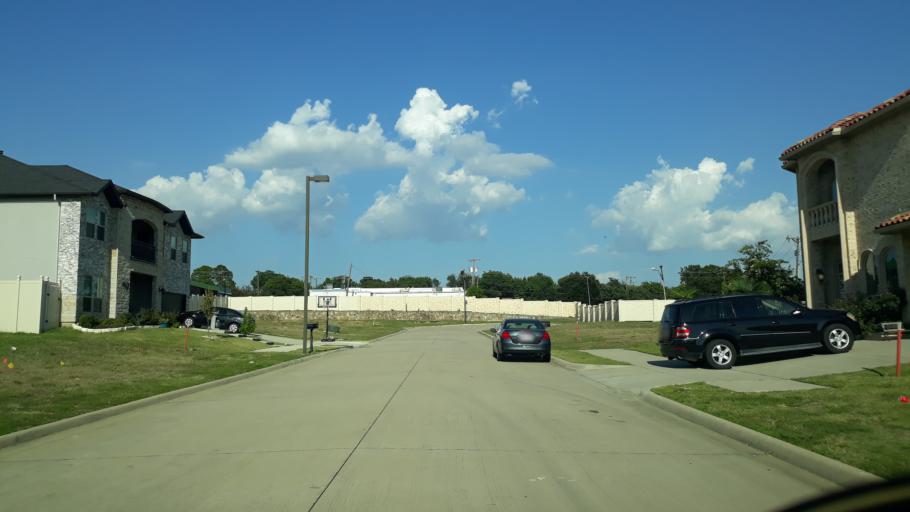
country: US
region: Texas
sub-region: Dallas County
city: Irving
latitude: 32.8474
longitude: -97.0102
